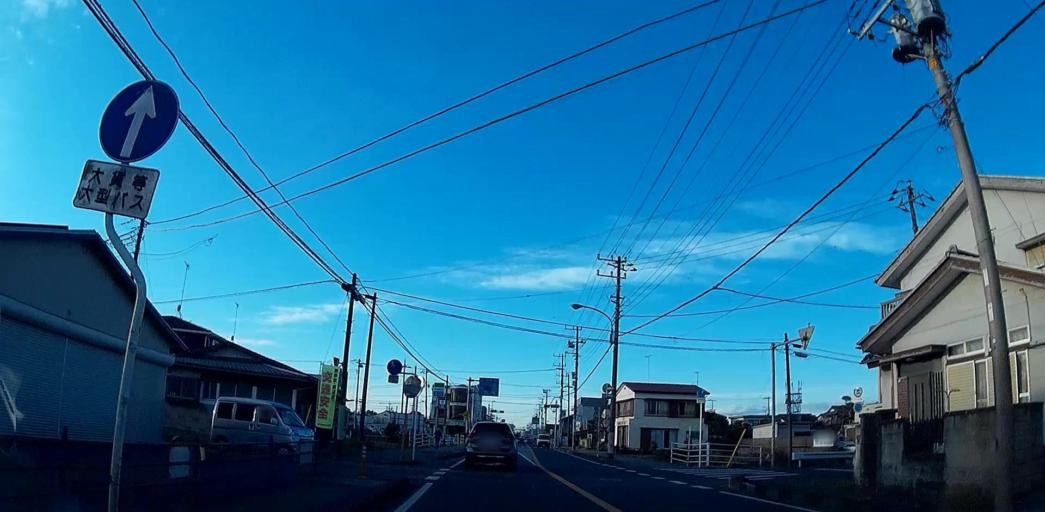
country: JP
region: Chiba
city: Omigawa
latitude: 35.8511
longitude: 140.6102
